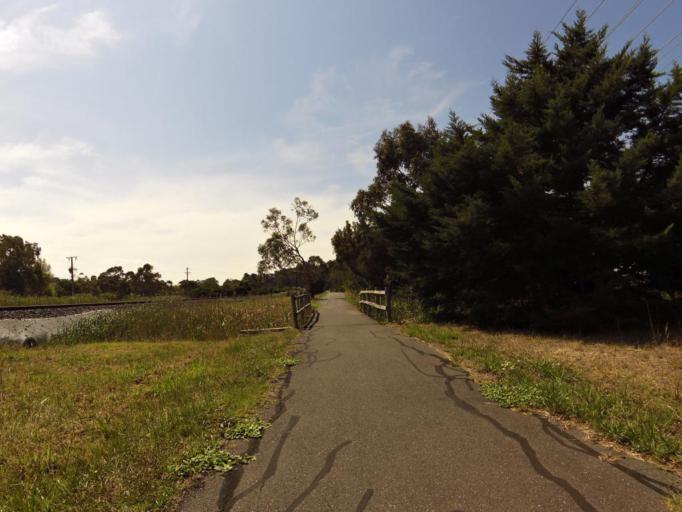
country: AU
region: Victoria
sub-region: Mornington Peninsula
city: Tyabb
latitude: -38.2685
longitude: 145.1895
